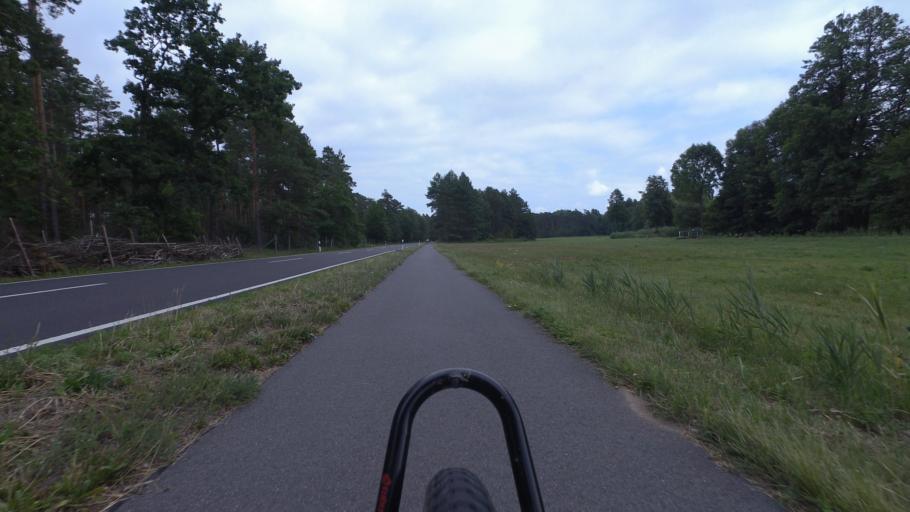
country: DE
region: Brandenburg
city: Sperenberg
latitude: 52.0852
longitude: 13.2981
